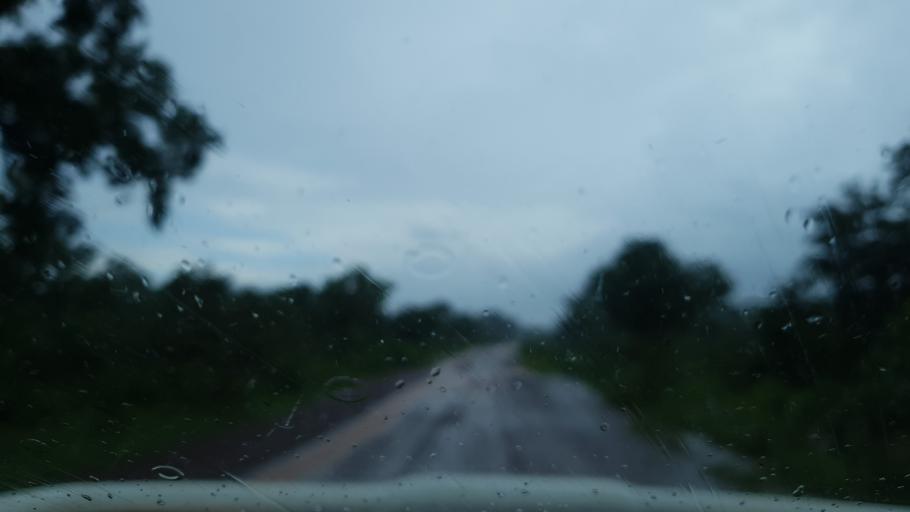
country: ML
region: Sikasso
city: Kolondieba
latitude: 11.6020
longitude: -6.6712
